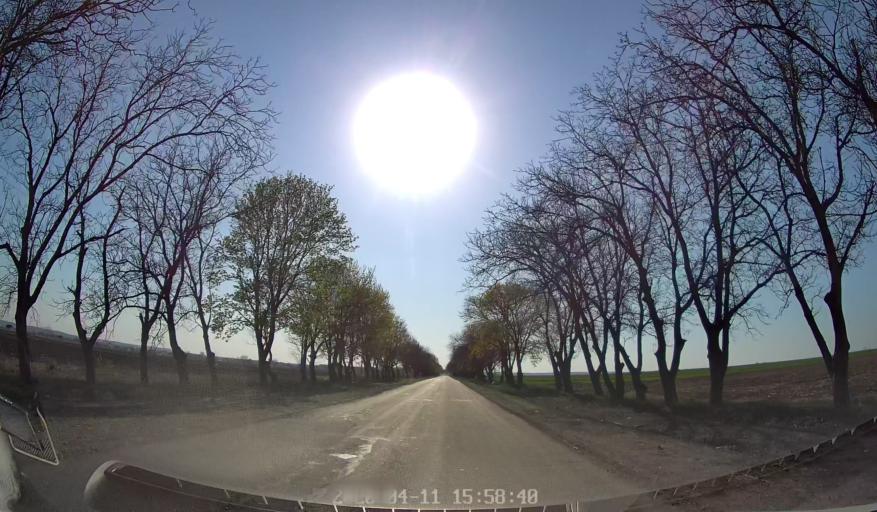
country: MD
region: Chisinau
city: Vadul lui Voda
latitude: 47.0845
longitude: 29.1530
